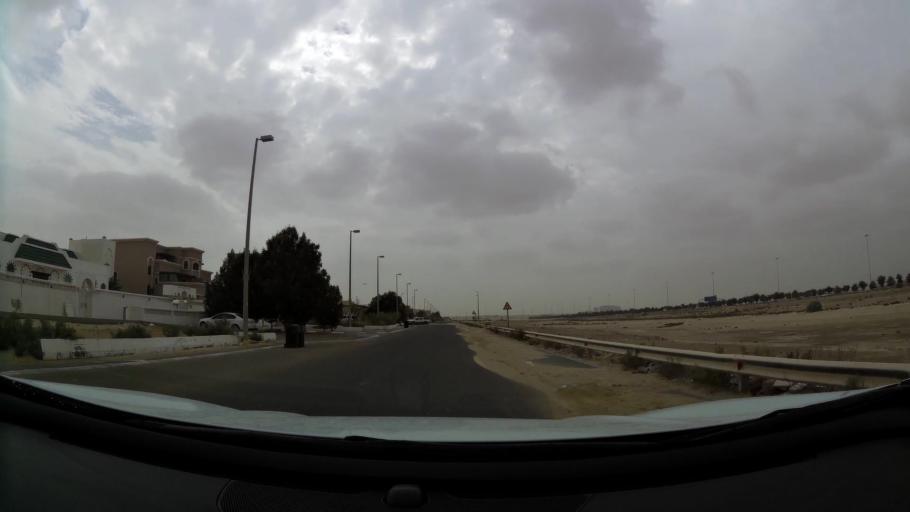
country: AE
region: Abu Dhabi
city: Abu Dhabi
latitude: 24.3476
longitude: 54.6443
